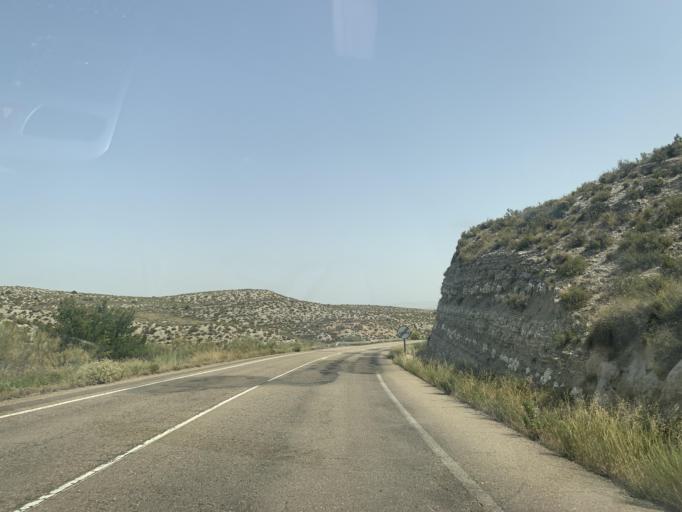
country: ES
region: Aragon
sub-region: Provincia de Zaragoza
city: El Burgo de Ebro
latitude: 41.5246
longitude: -0.7037
